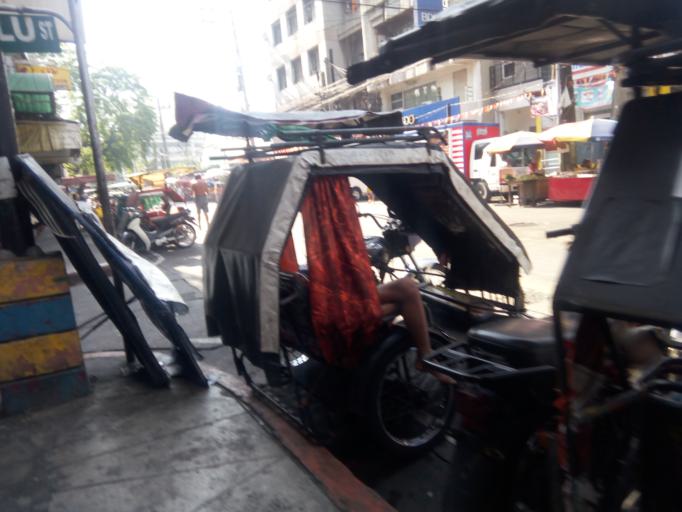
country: PH
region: Metro Manila
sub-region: City of Manila
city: Manila
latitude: 14.6078
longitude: 120.9843
